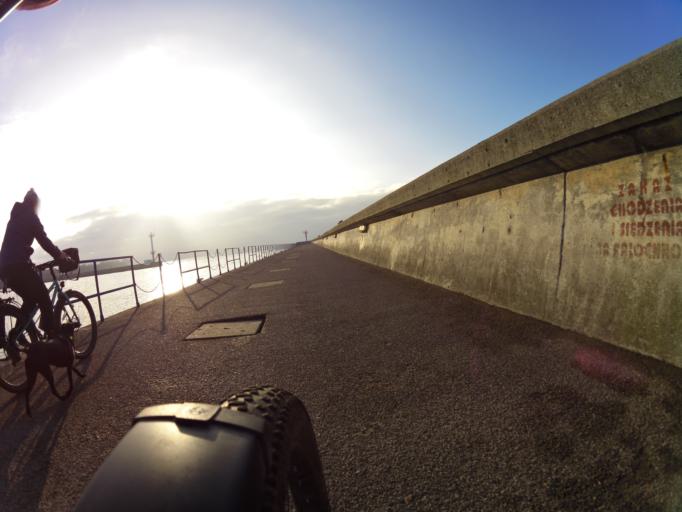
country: PL
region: Pomeranian Voivodeship
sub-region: Powiat pucki
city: Hel
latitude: 54.6011
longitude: 18.7992
